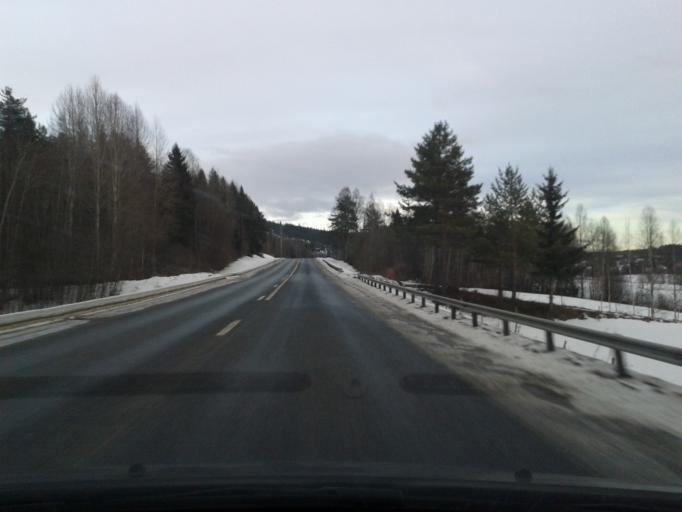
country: SE
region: Vaesternorrland
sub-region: Solleftea Kommun
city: Solleftea
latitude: 63.3515
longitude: 17.0496
